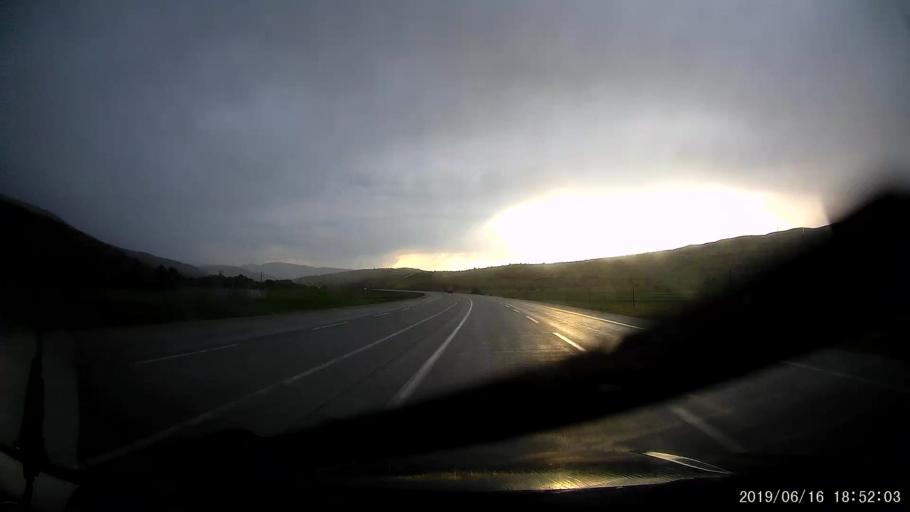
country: TR
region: Erzincan
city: Catalcam
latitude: 39.9026
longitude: 38.9120
